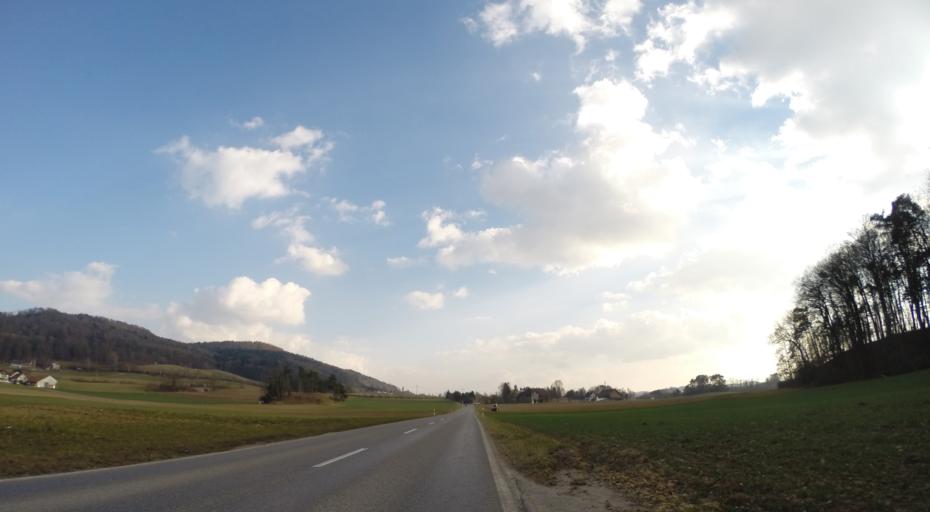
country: CH
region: Thurgau
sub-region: Frauenfeld District
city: Diessenhofen
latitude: 47.6565
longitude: 8.7830
